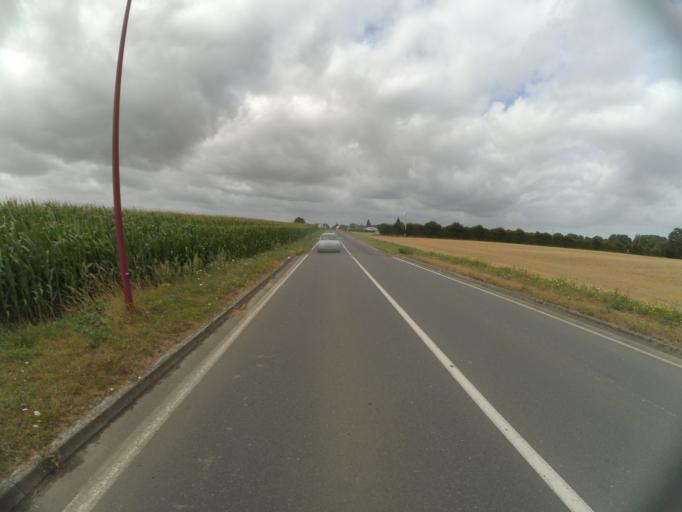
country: FR
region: Pays de la Loire
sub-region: Departement de Maine-et-Loire
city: Villedieu-la-Blouere
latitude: 47.1399
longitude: -1.0726
